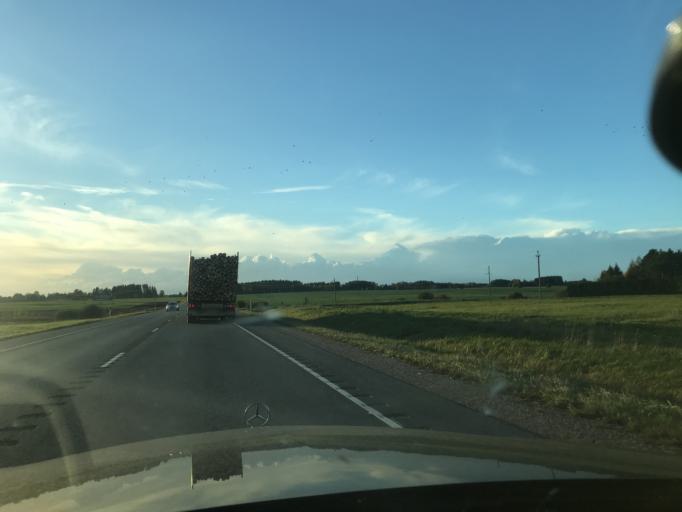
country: EE
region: Vorumaa
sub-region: Voru linn
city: Voru
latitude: 57.8664
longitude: 26.9534
